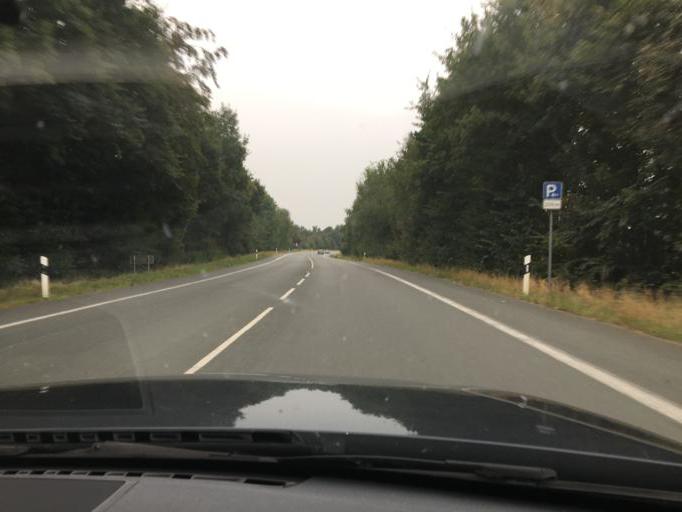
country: DE
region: North Rhine-Westphalia
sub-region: Regierungsbezirk Munster
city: Ladbergen
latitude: 52.1255
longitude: 7.7229
